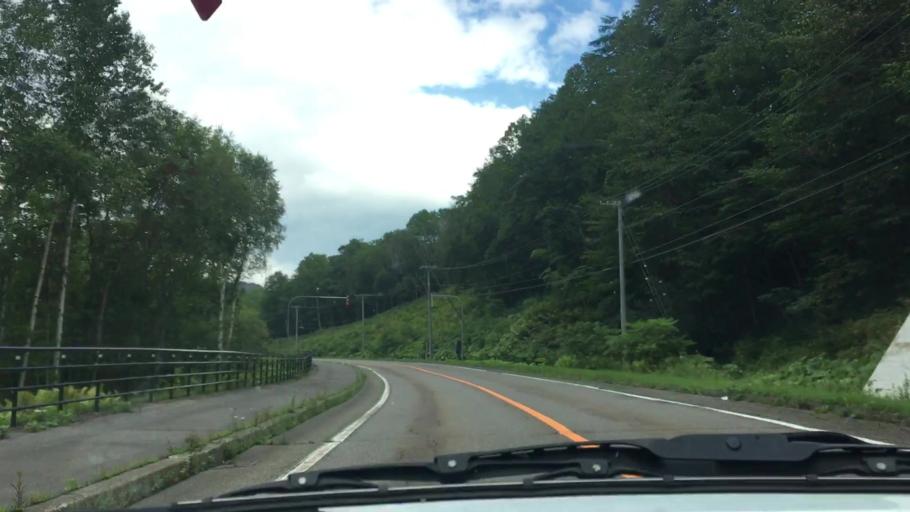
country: JP
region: Hokkaido
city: Otofuke
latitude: 43.3611
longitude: 143.2478
